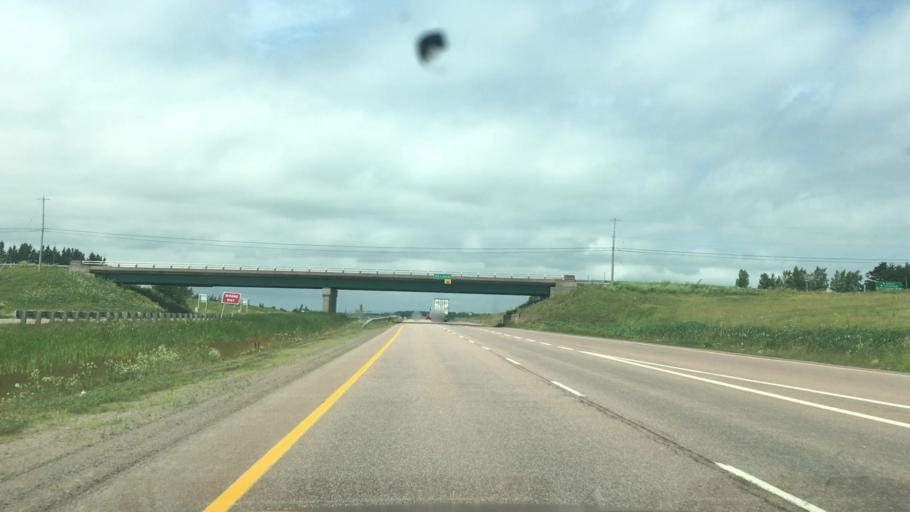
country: CA
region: Nova Scotia
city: Amherst
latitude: 45.8525
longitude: -64.2542
